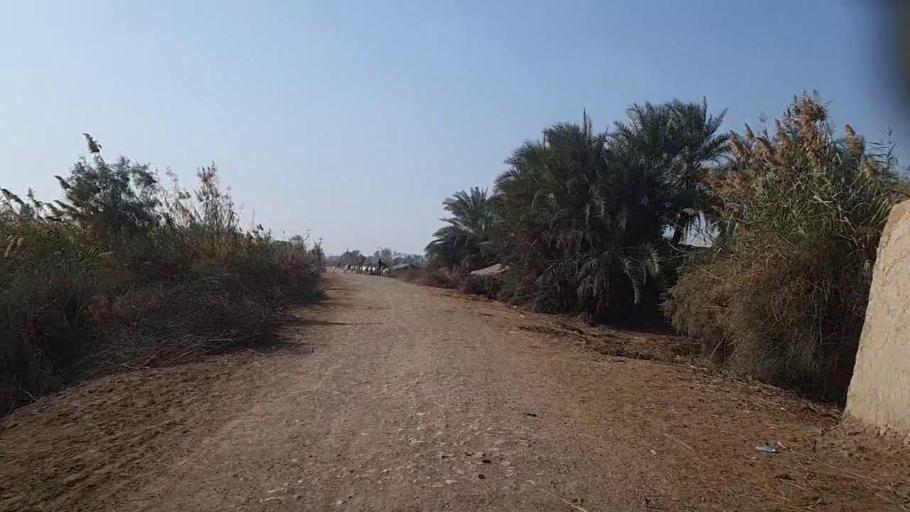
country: PK
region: Sindh
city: Mirpur Mathelo
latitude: 27.9036
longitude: 69.6170
